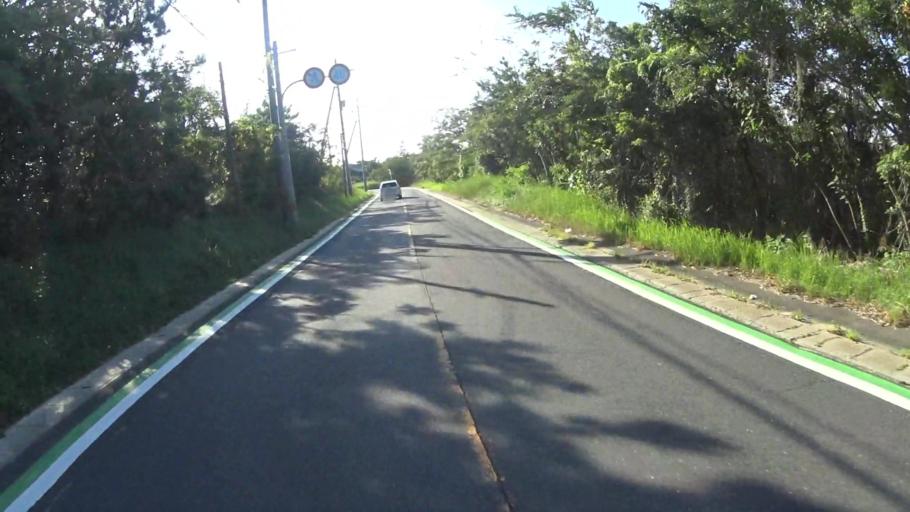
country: JP
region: Hyogo
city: Toyooka
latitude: 35.6564
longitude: 134.9588
